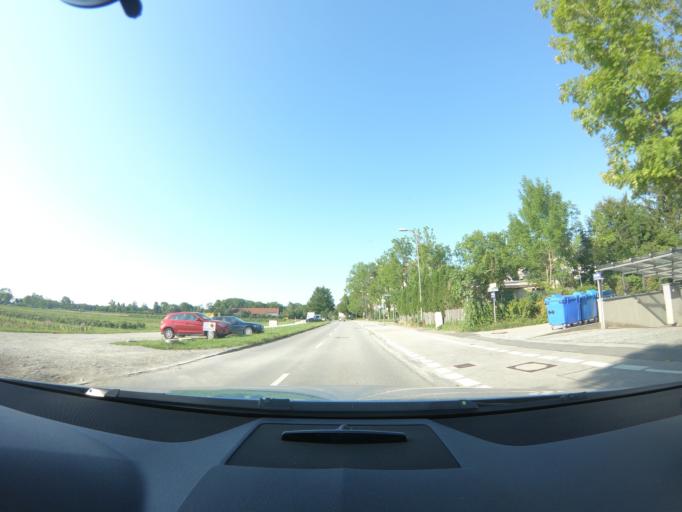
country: DE
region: Bavaria
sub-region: Upper Bavaria
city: Unterhaching
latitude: 48.0906
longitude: 11.6244
